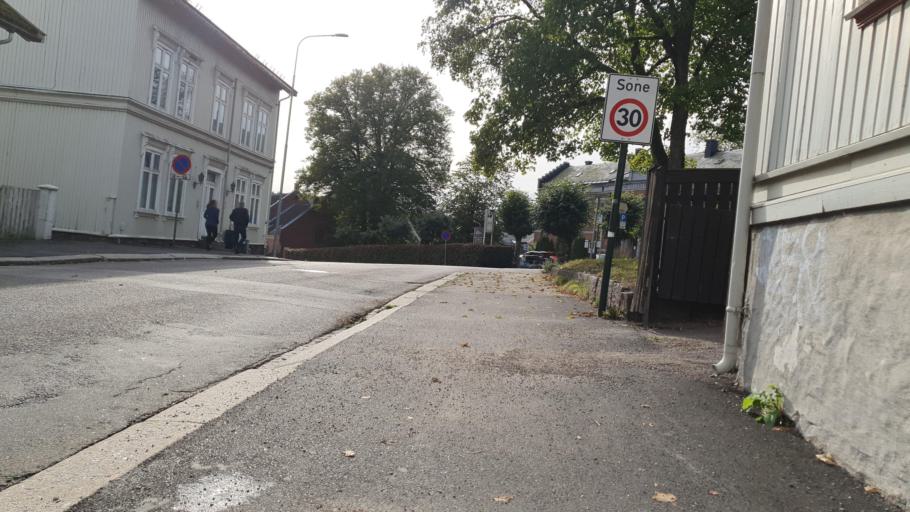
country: NO
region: Vestfold
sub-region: Tonsberg
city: Tonsberg
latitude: 59.2668
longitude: 10.4146
